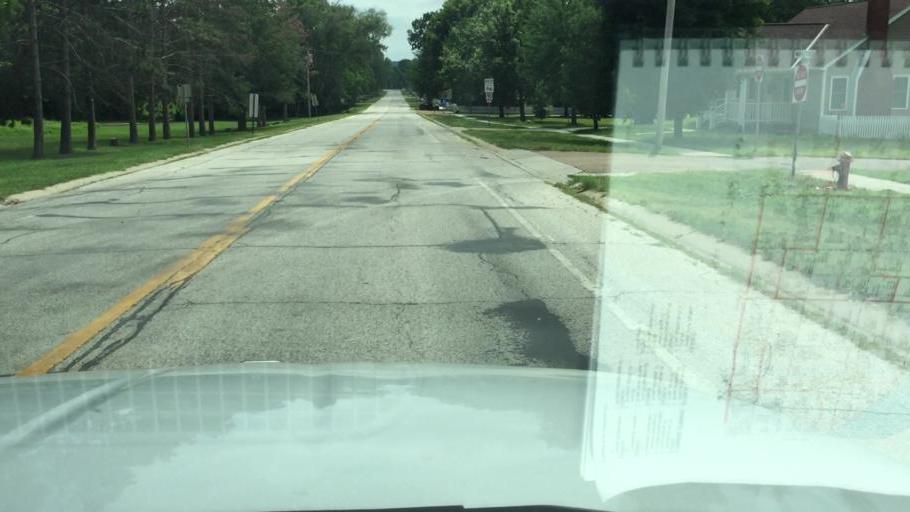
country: US
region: Illinois
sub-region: Hancock County
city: Nauvoo
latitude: 40.5477
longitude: -91.3866
